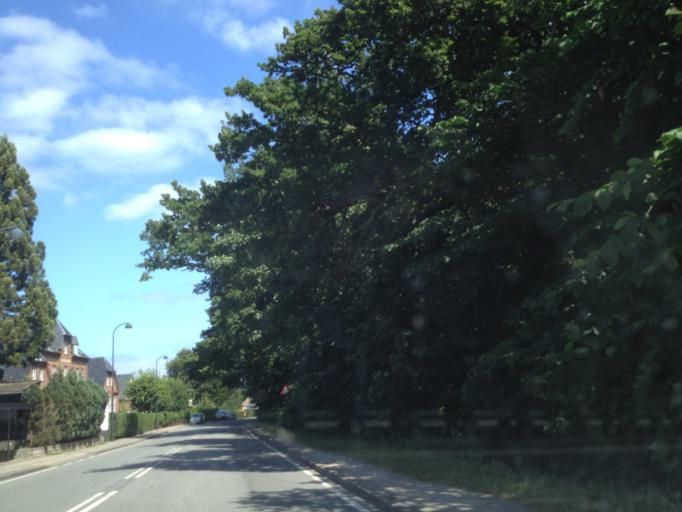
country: DK
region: Capital Region
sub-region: Rudersdal Kommune
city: Trorod
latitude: 55.8467
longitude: 12.5636
